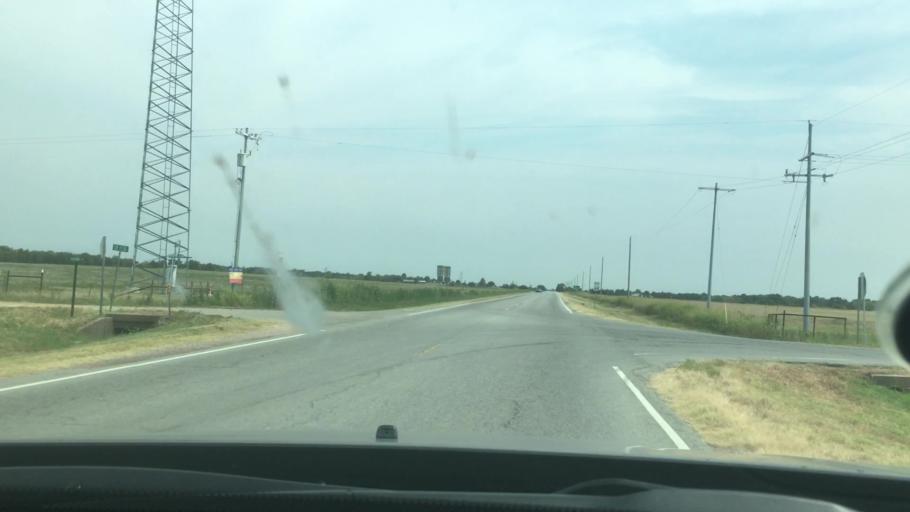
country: US
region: Oklahoma
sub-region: Coal County
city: Coalgate
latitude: 34.5051
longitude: -96.4070
